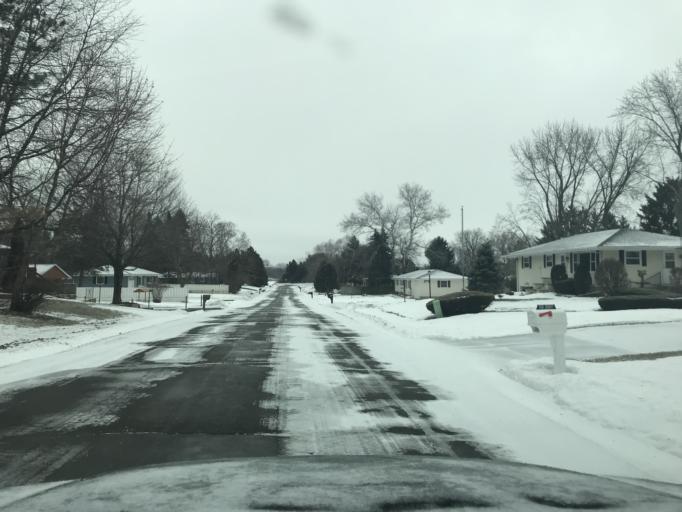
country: US
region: Wisconsin
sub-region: Dane County
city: Cottage Grove
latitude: 43.0961
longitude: -89.2360
